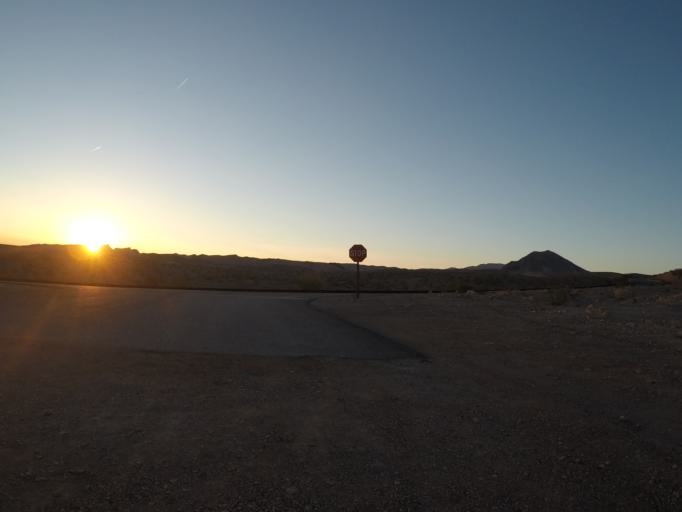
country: US
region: Nevada
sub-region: Clark County
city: Henderson
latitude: 36.1253
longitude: -114.9034
